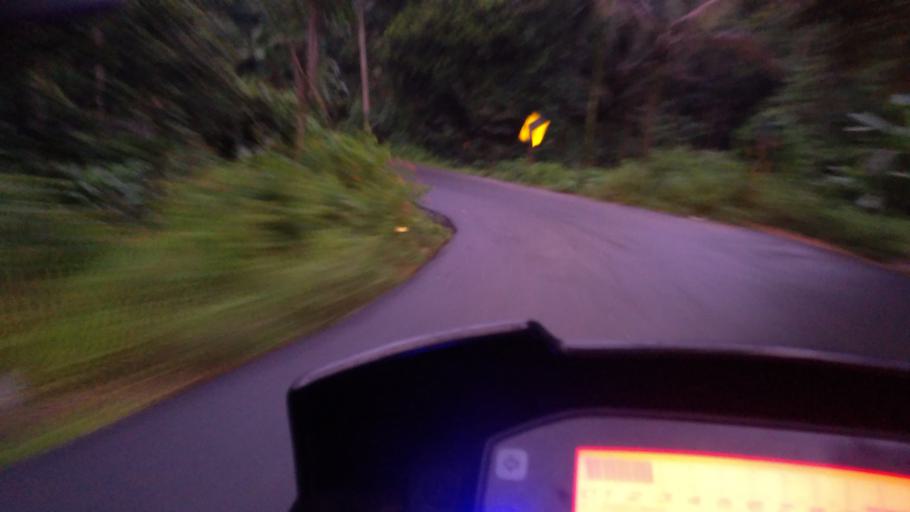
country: IN
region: Kerala
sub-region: Idukki
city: Munnar
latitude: 9.9630
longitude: 77.0702
